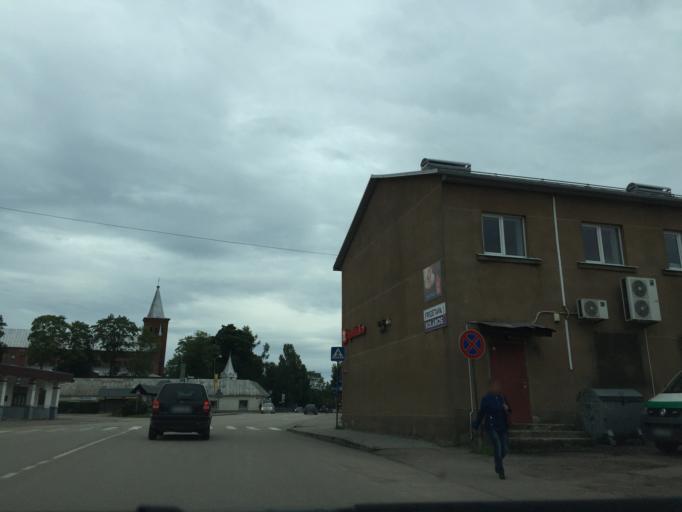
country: LV
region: Preilu Rajons
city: Preili
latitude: 56.2945
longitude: 26.7231
